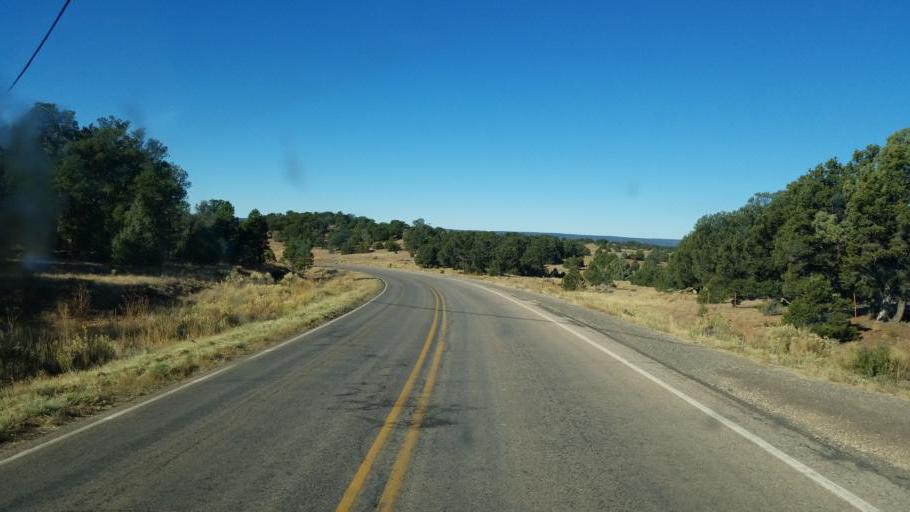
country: US
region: New Mexico
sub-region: McKinley County
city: Navajo
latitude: 36.0398
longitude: -108.9749
